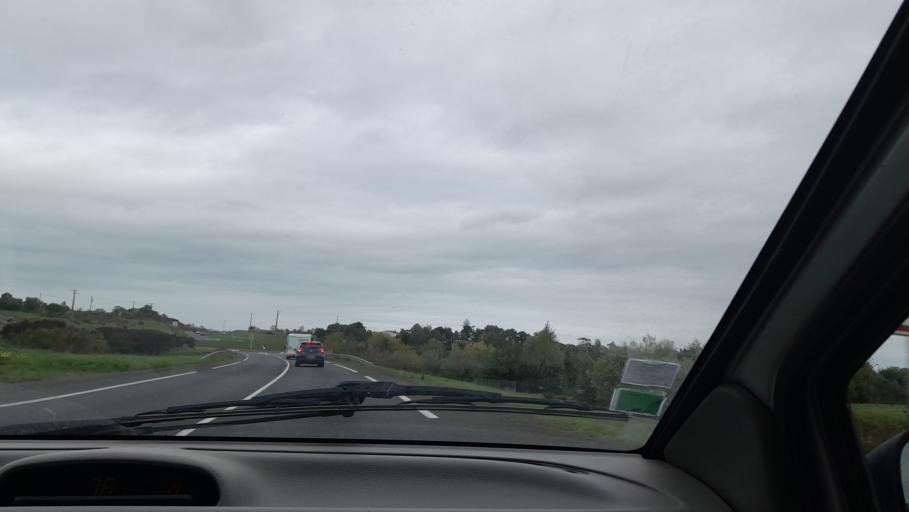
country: FR
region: Pays de la Loire
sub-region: Departement de la Loire-Atlantique
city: Saint-Gereon
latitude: 47.3851
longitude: -1.2017
